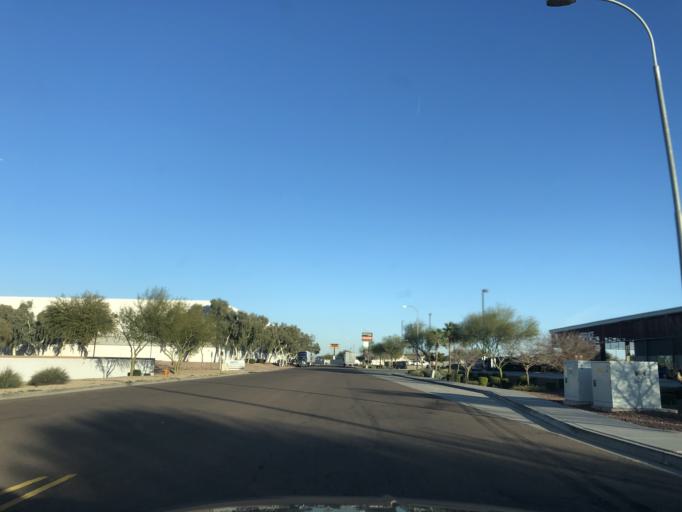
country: US
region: Arizona
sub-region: Maricopa County
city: Tolleson
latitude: 33.4579
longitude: -112.2709
